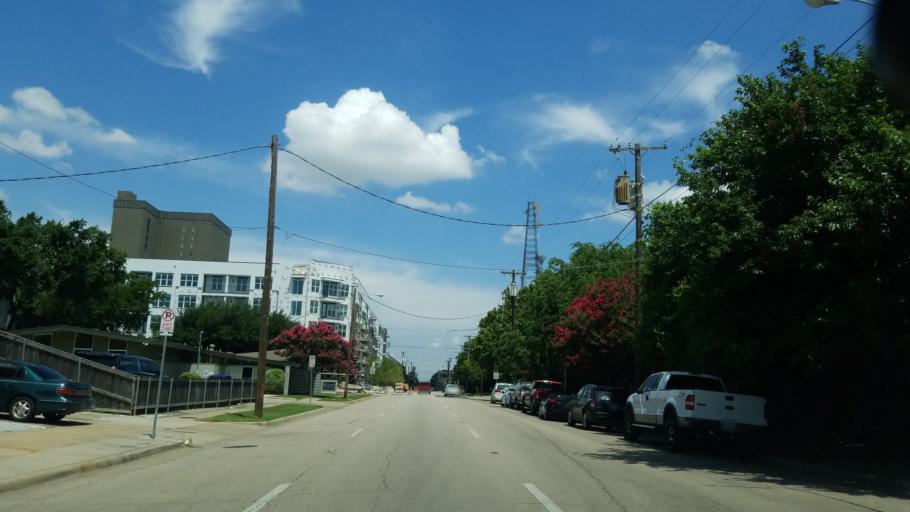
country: US
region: Texas
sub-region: Dallas County
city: Dallas
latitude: 32.7958
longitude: -96.7758
